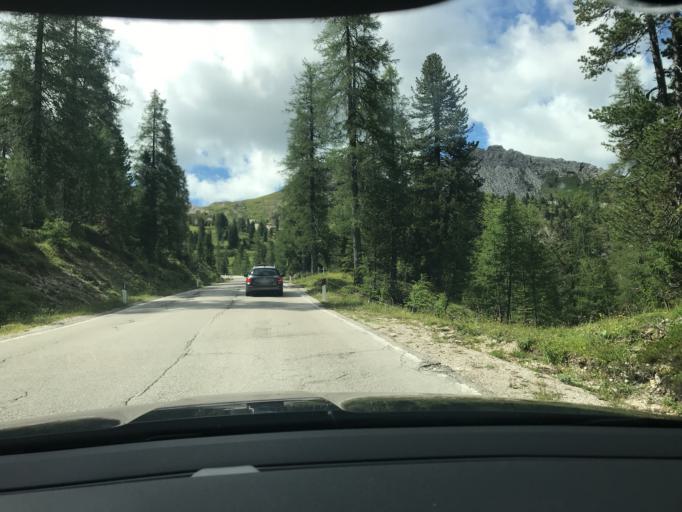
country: IT
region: Veneto
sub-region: Provincia di Belluno
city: Livinallongo del Col di Lana
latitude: 46.5385
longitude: 11.9847
